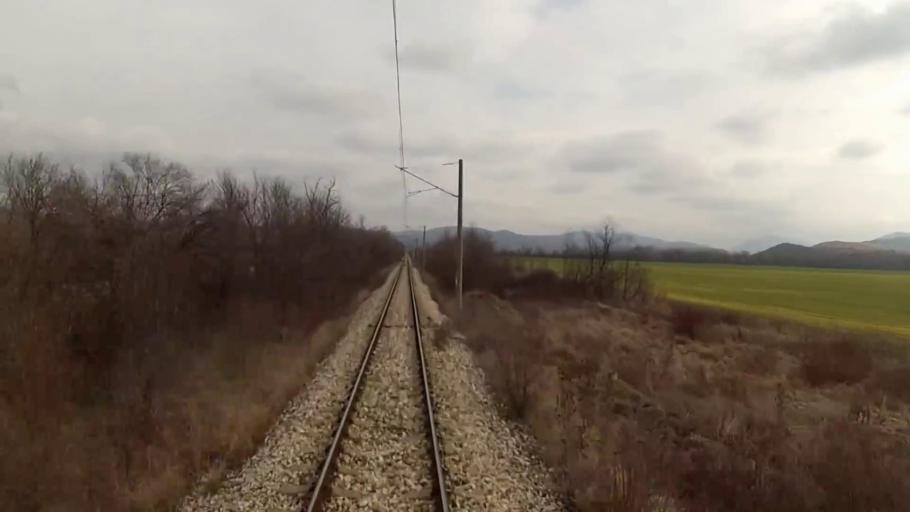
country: BG
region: Sofiya
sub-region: Obshtina Gorna Malina
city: Gorna Malina
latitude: 42.7173
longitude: 23.7514
